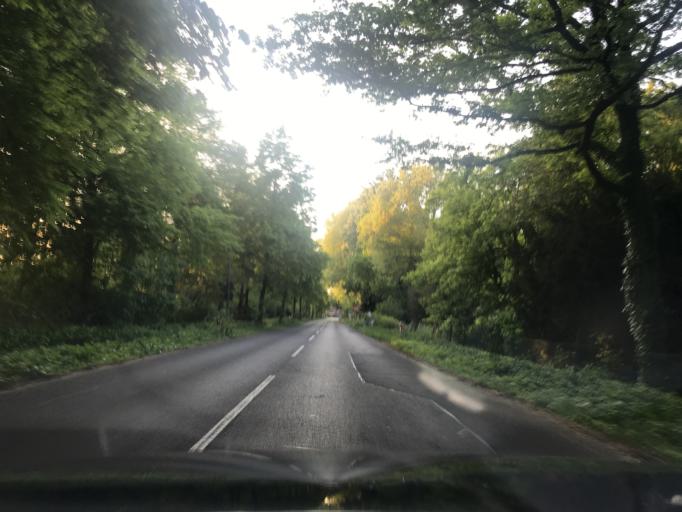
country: DE
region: North Rhine-Westphalia
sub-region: Regierungsbezirk Dusseldorf
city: Korschenbroich
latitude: 51.2475
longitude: 6.4795
